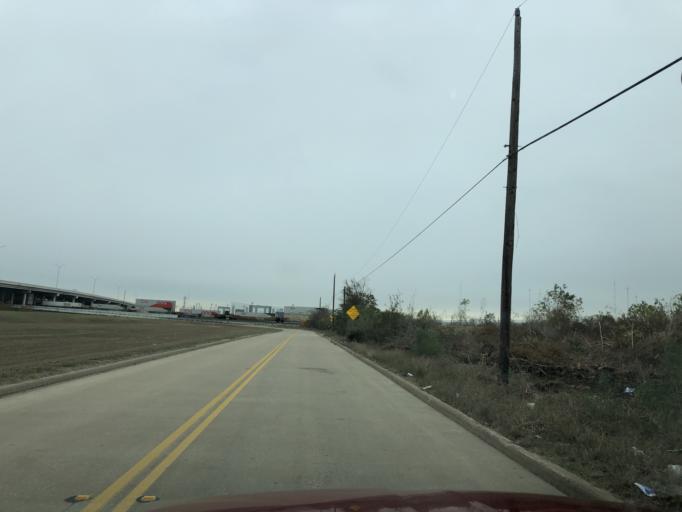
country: US
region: Texas
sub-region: Fort Bend County
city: Missouri City
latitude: 29.6279
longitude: -95.5212
